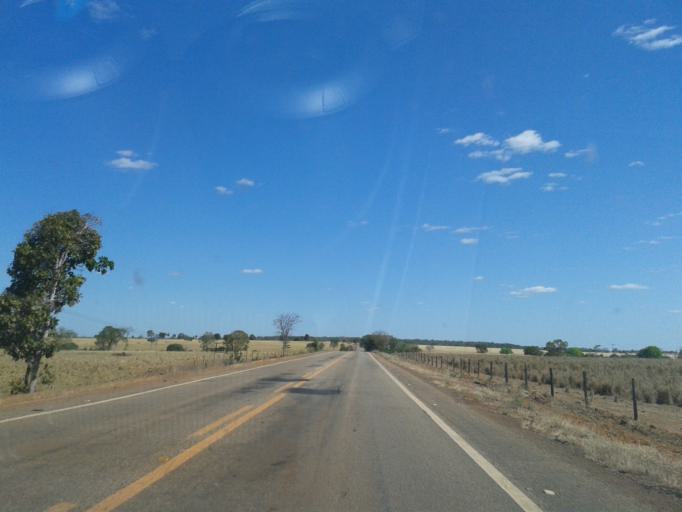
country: BR
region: Goias
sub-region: Sao Miguel Do Araguaia
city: Sao Miguel do Araguaia
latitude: -13.4436
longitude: -50.2909
